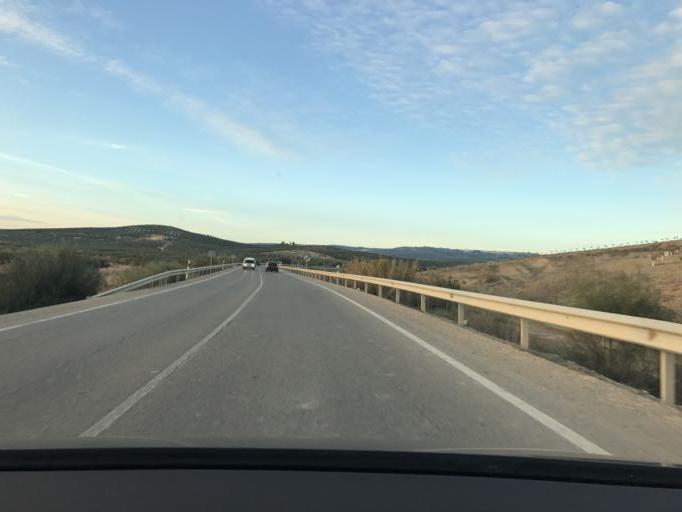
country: ES
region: Andalusia
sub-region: Provincia de Jaen
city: Ubeda
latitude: 37.9417
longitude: -3.3582
